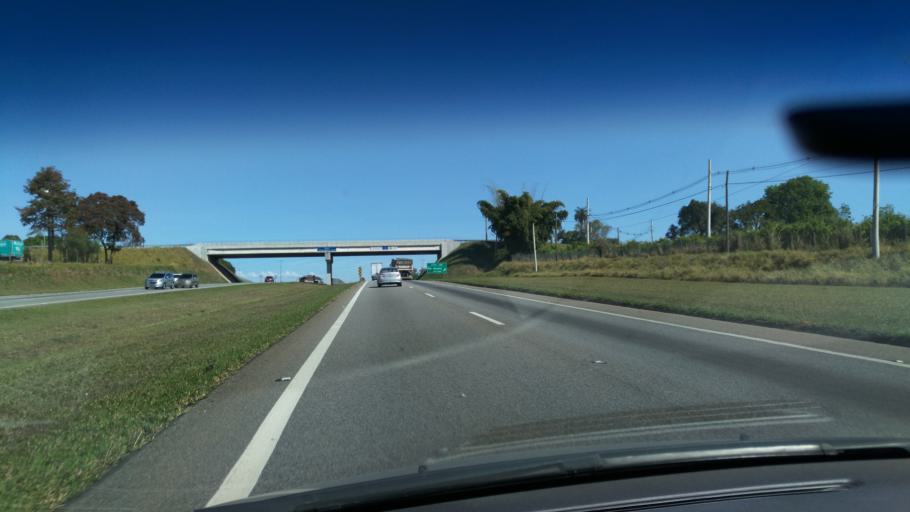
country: BR
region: Sao Paulo
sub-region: Jaguariuna
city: Jaguariuna
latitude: -22.6798
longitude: -47.0064
